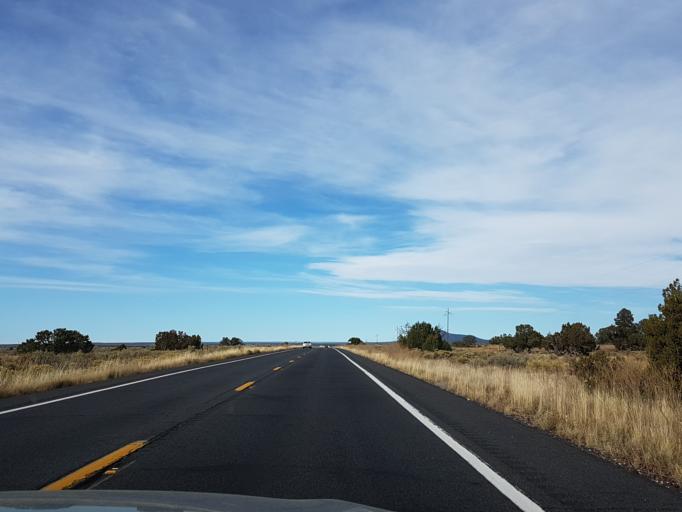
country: US
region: Arizona
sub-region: Coconino County
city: Grand Canyon Village
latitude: 35.6854
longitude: -112.1349
